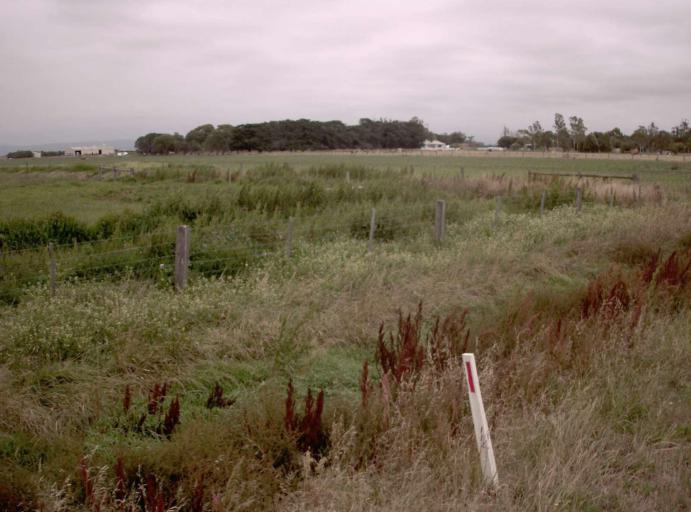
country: AU
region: Victoria
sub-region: Wellington
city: Heyfield
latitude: -38.0803
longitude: 146.7712
